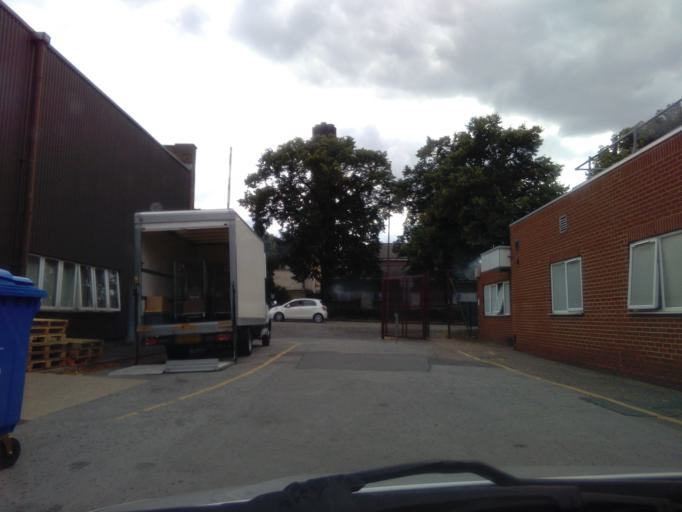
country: GB
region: England
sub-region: Bedford
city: Bedford
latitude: 52.1287
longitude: -0.4696
